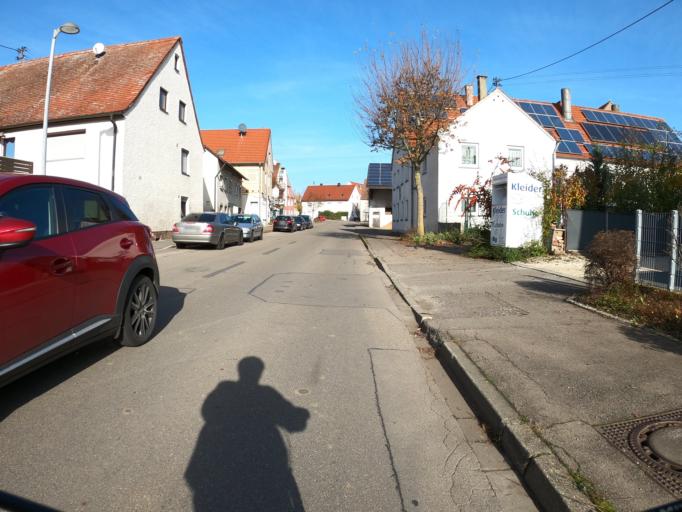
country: DE
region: Bavaria
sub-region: Swabia
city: Nersingen
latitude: 48.4581
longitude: 10.1047
